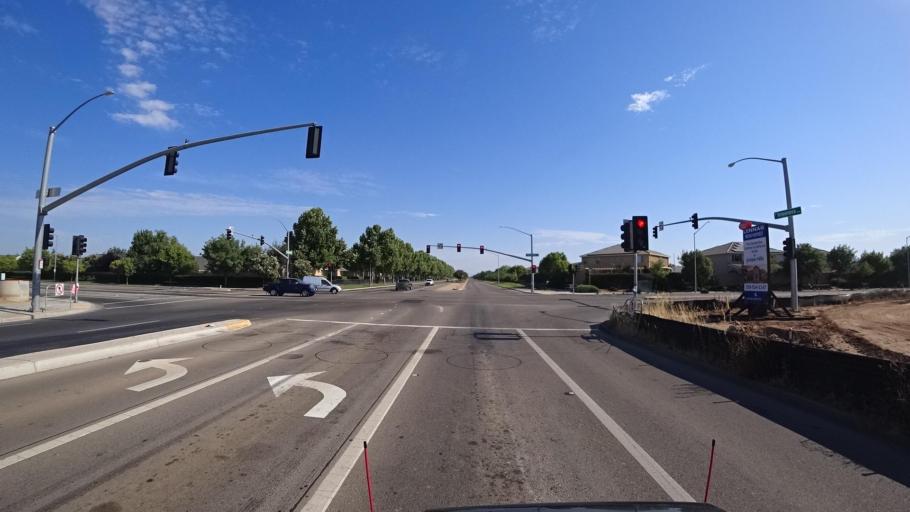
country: US
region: California
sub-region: Fresno County
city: Tarpey Village
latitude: 36.7791
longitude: -119.6640
